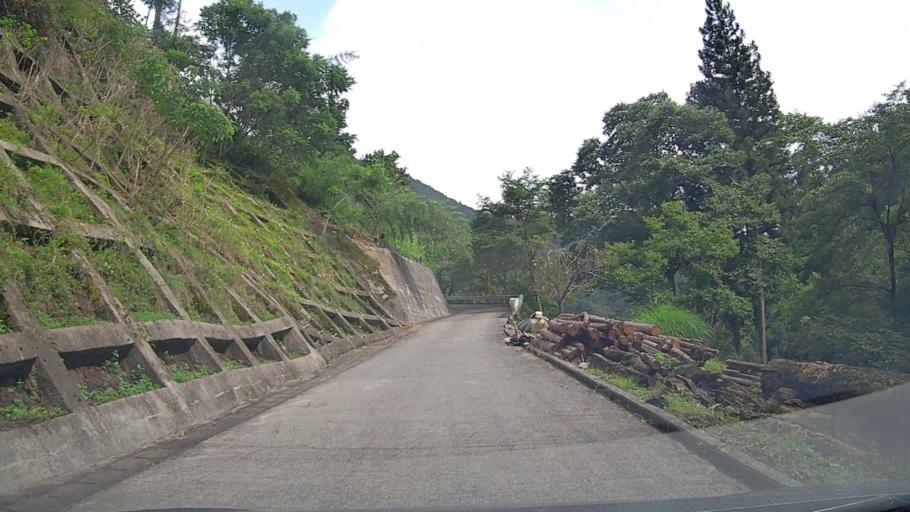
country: JP
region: Yamanashi
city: Uenohara
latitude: 35.7504
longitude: 139.0805
